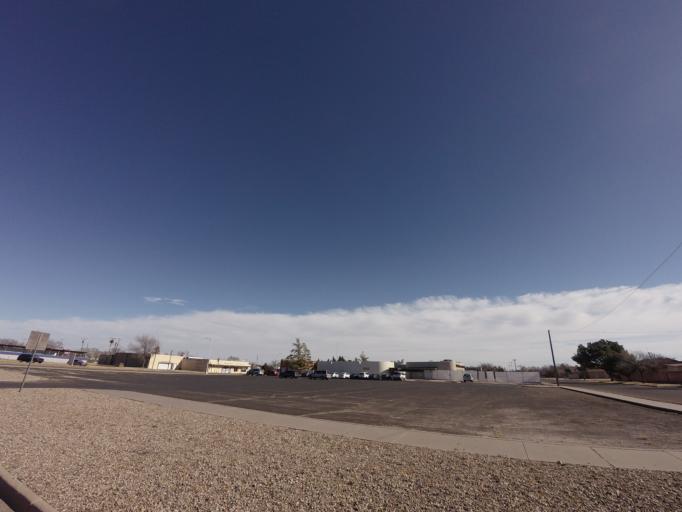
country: US
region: New Mexico
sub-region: Curry County
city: Clovis
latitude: 34.4040
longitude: -103.2167
